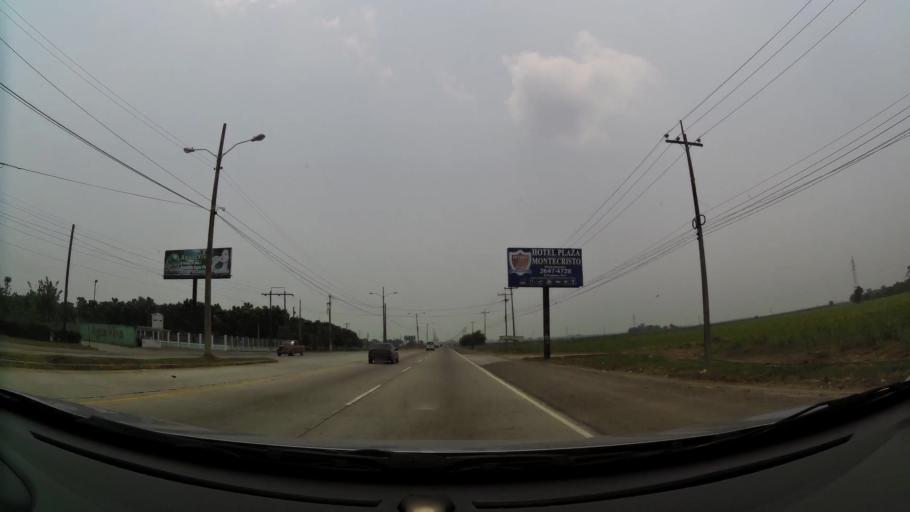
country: HN
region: Cortes
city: La Lima
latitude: 15.4117
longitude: -87.8709
